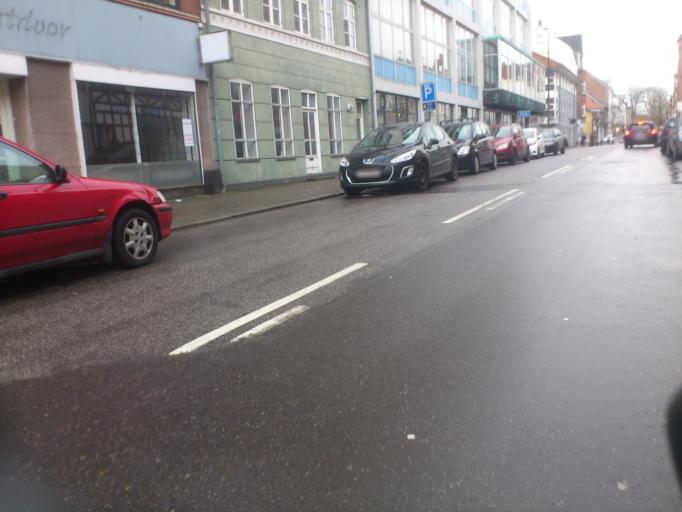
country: DK
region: South Denmark
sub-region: Fredericia Kommune
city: Fredericia
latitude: 55.5671
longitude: 9.7587
